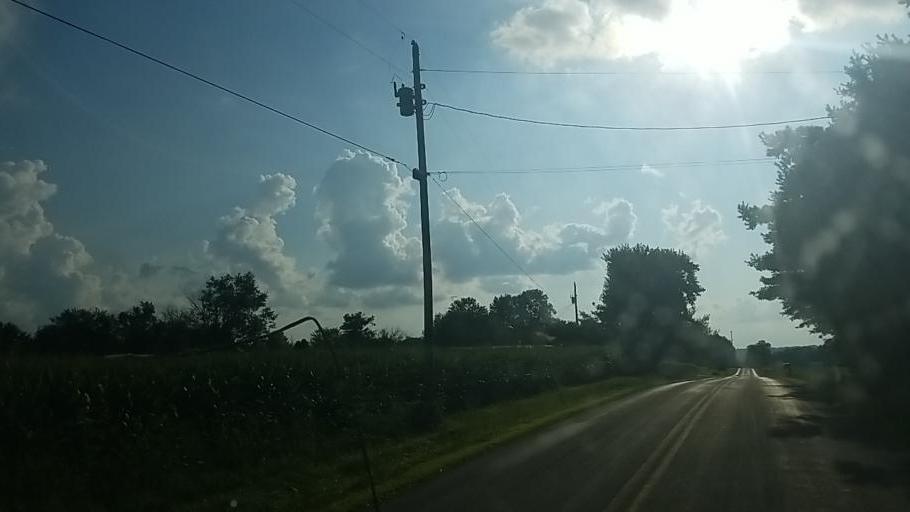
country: US
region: Ohio
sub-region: Ashland County
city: Ashland
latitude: 40.8713
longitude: -82.2013
